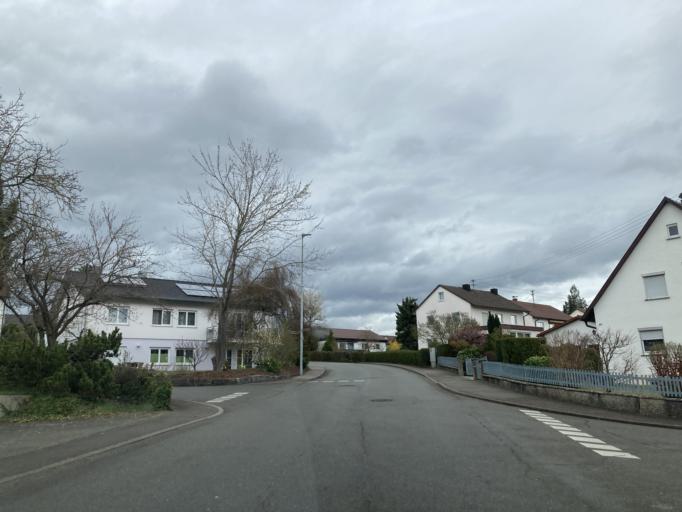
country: DE
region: Baden-Wuerttemberg
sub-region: Tuebingen Region
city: Rottenburg
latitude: 48.5066
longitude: 8.9692
